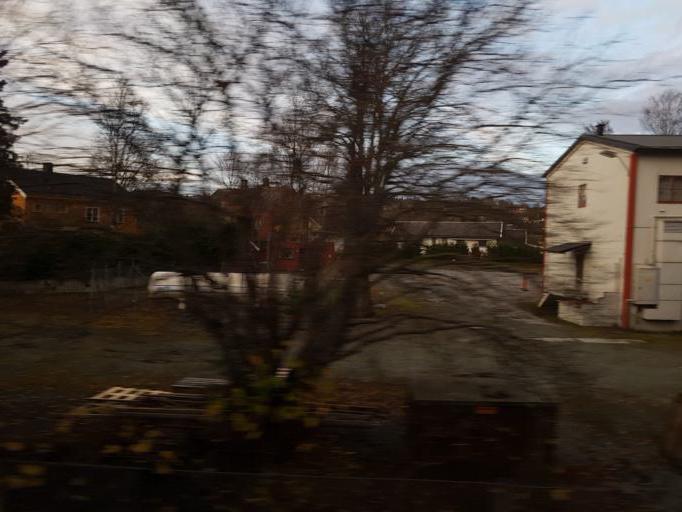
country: NO
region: Sor-Trondelag
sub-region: Melhus
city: Melhus
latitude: 63.2879
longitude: 10.2786
